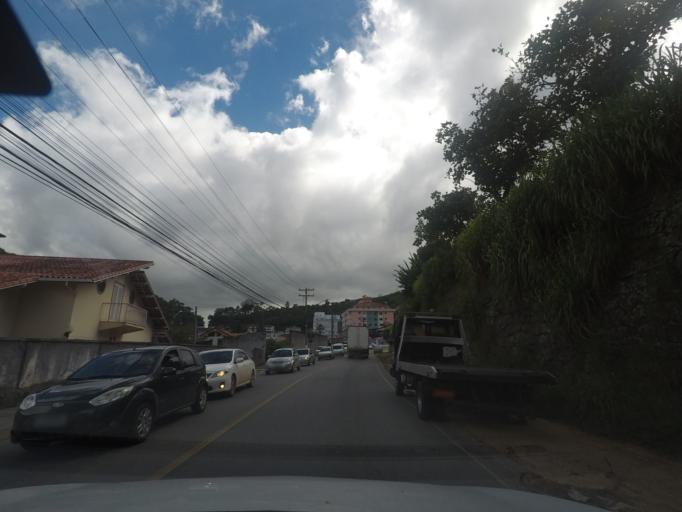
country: BR
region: Rio de Janeiro
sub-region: Teresopolis
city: Teresopolis
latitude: -22.4007
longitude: -42.9631
